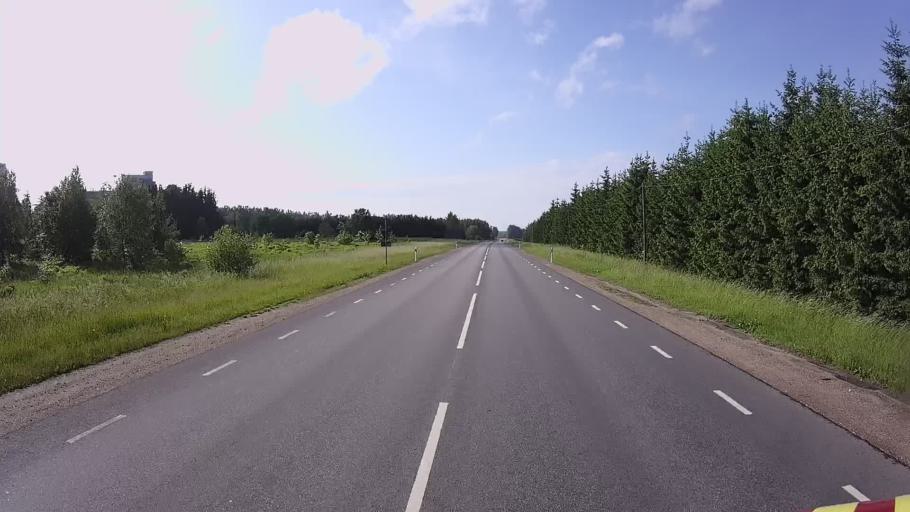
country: EE
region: Viljandimaa
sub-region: Viljandi linn
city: Viljandi
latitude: 58.3542
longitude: 25.5598
